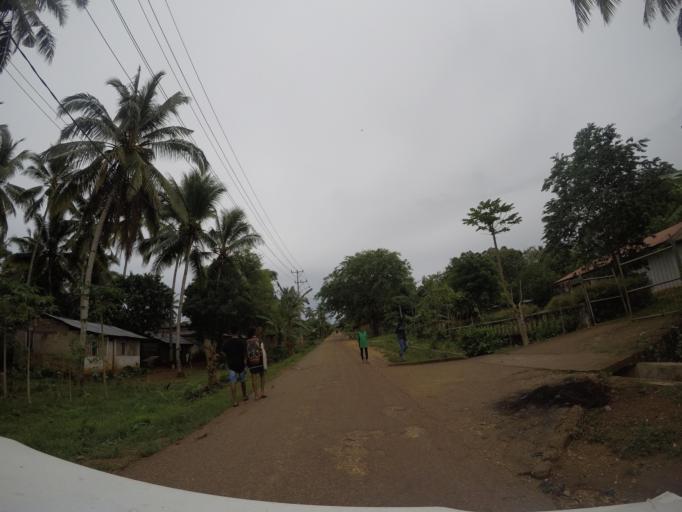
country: TL
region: Lautem
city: Lospalos
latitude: -8.5301
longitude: 126.9982
